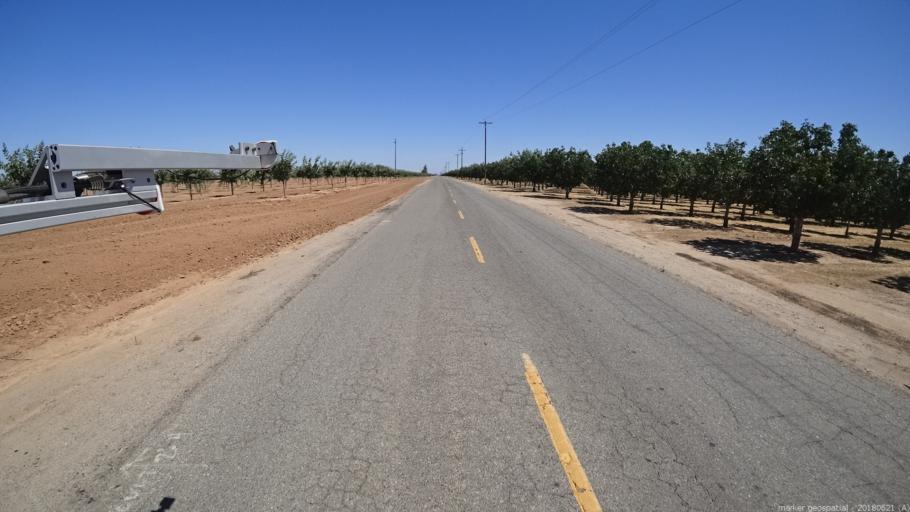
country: US
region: California
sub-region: Madera County
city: Parksdale
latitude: 36.8985
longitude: -119.9394
